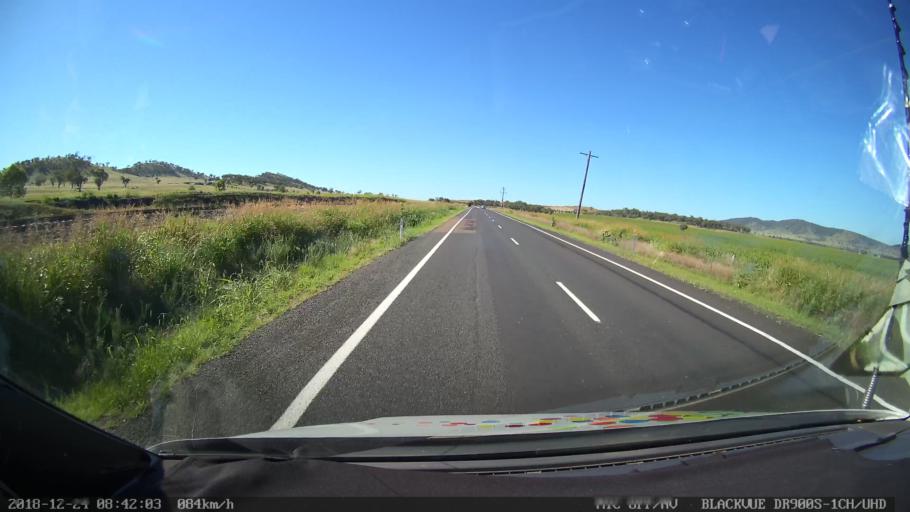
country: AU
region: New South Wales
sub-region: Liverpool Plains
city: Quirindi
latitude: -31.3693
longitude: 150.6437
